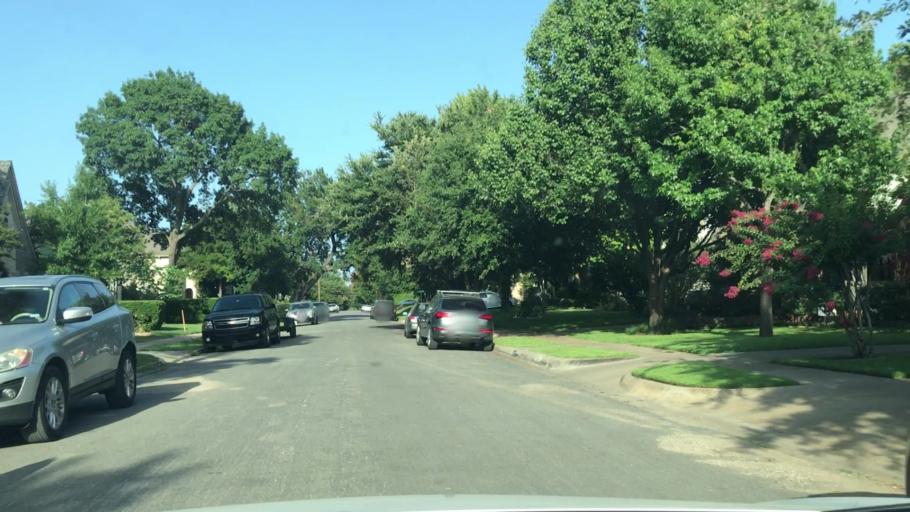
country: US
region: Texas
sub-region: Dallas County
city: Highland Park
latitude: 32.8221
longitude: -96.7598
